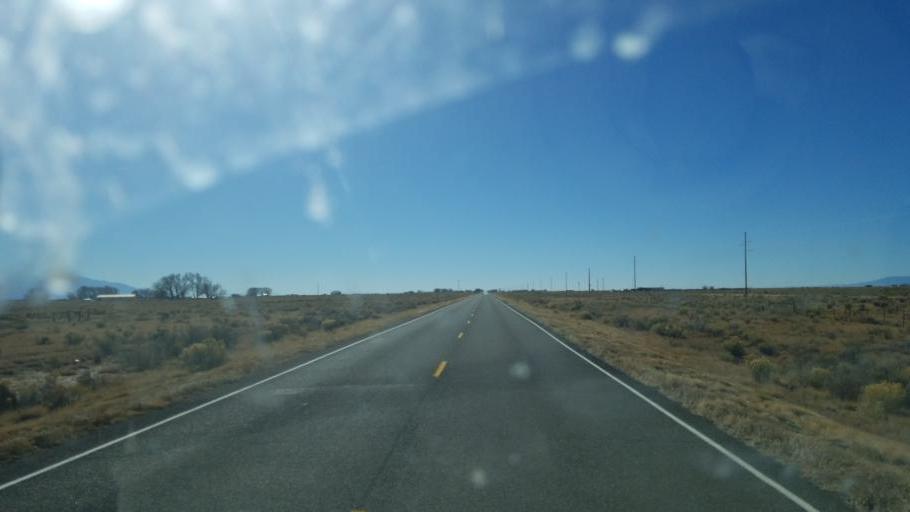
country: US
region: Colorado
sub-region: Saguache County
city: Saguache
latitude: 38.0462
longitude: -105.9138
